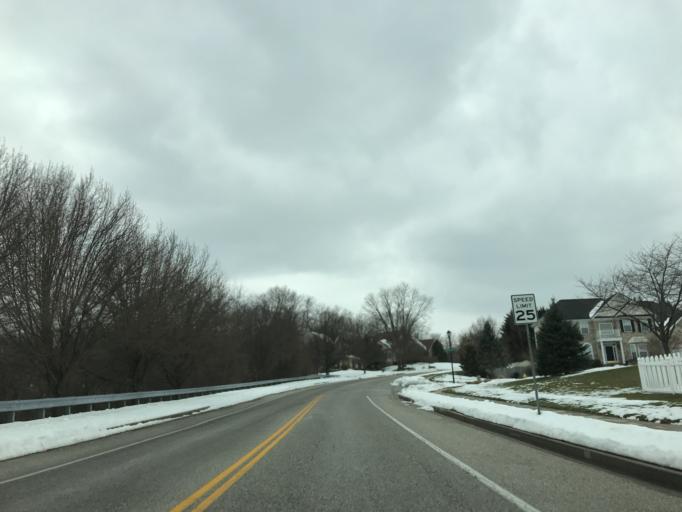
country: US
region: Maryland
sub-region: Harford County
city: Bel Air North
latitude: 39.5614
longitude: -76.3920
